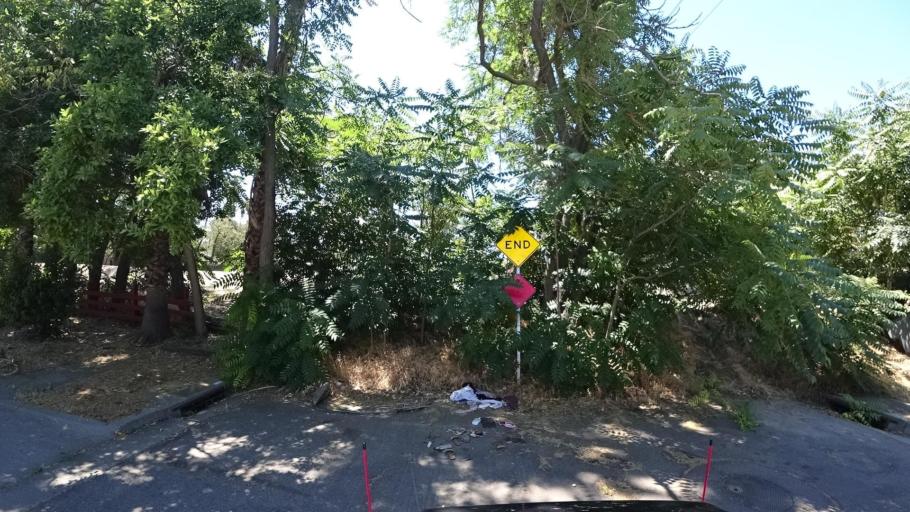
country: US
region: California
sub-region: Fresno County
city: Fresno
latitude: 36.7833
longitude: -119.7973
